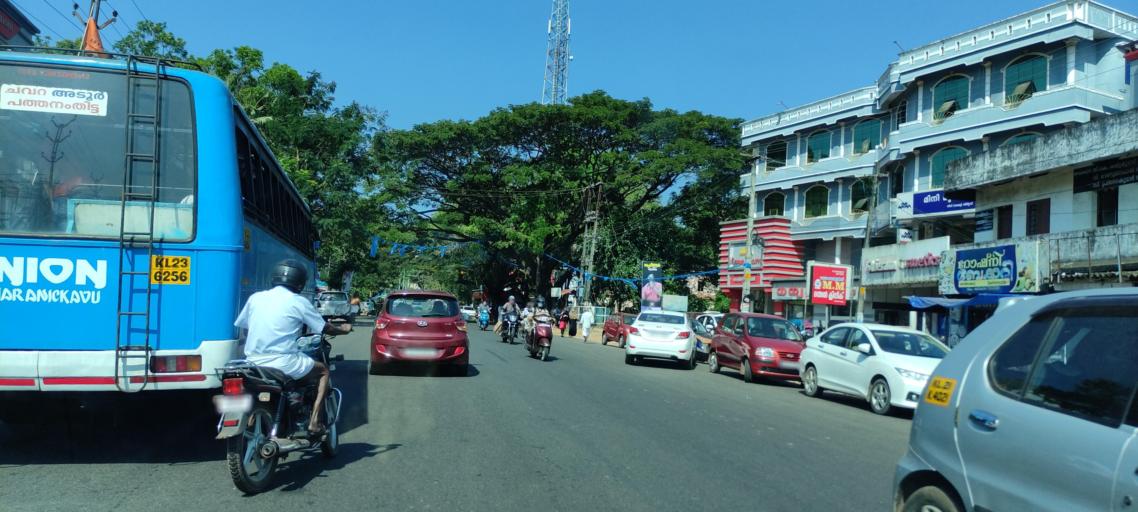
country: IN
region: Kerala
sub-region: Kollam
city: Panmana
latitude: 9.0434
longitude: 76.6254
